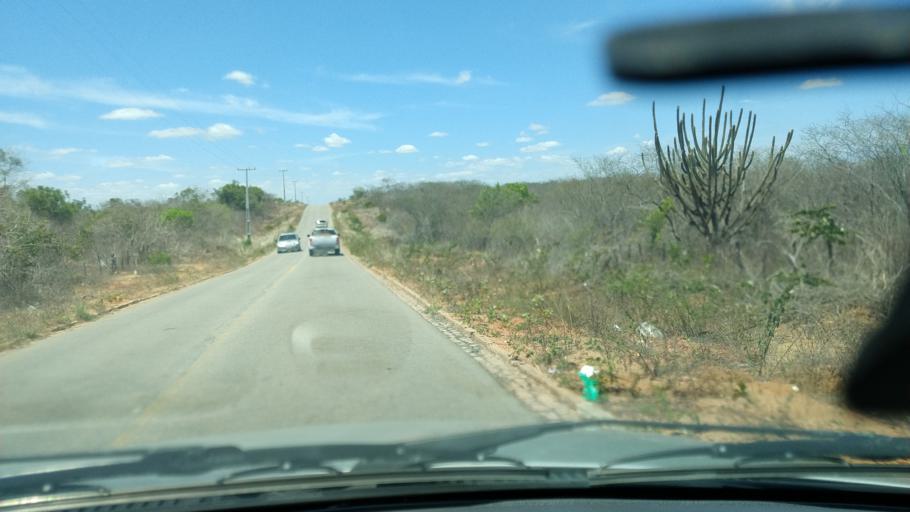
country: BR
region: Rio Grande do Norte
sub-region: Sao Paulo Do Potengi
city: Sao Paulo do Potengi
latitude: -5.9145
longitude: -35.5901
